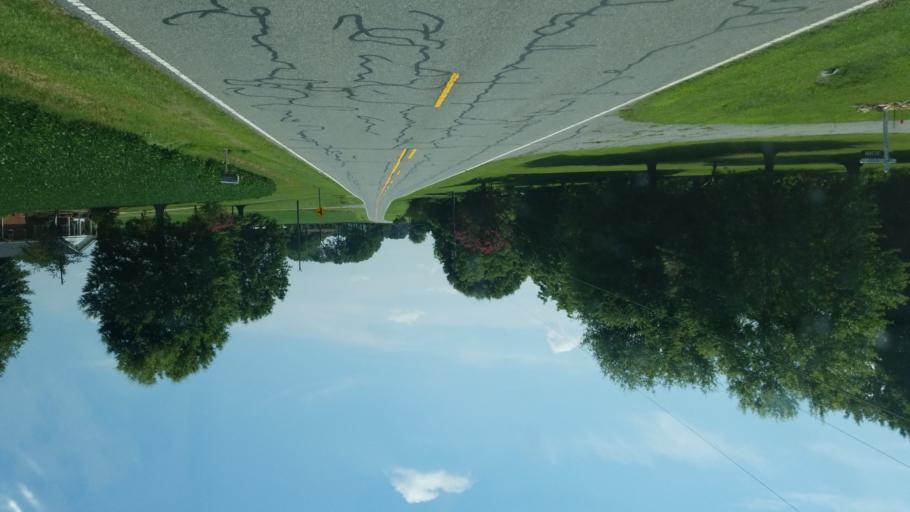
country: US
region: North Carolina
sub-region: Gaston County
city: Cherryville
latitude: 35.4786
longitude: -81.4436
